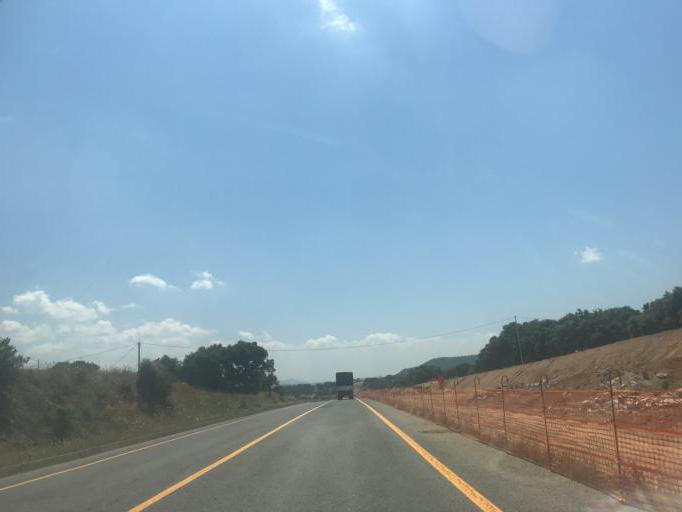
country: IT
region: Sardinia
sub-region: Provincia di Olbia-Tempio
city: Monti
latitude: 40.7870
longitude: 9.2558
